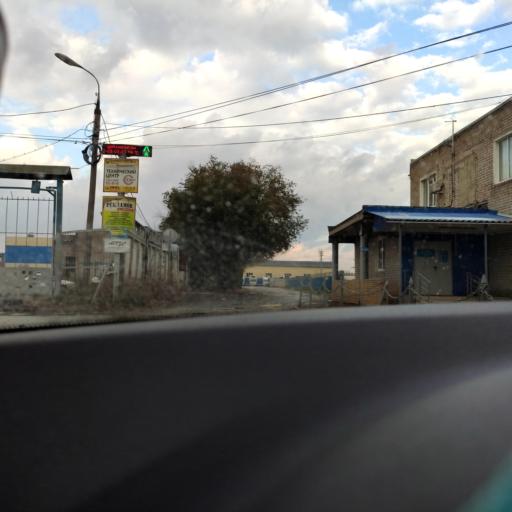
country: RU
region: Samara
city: Samara
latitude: 53.2013
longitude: 50.2550
